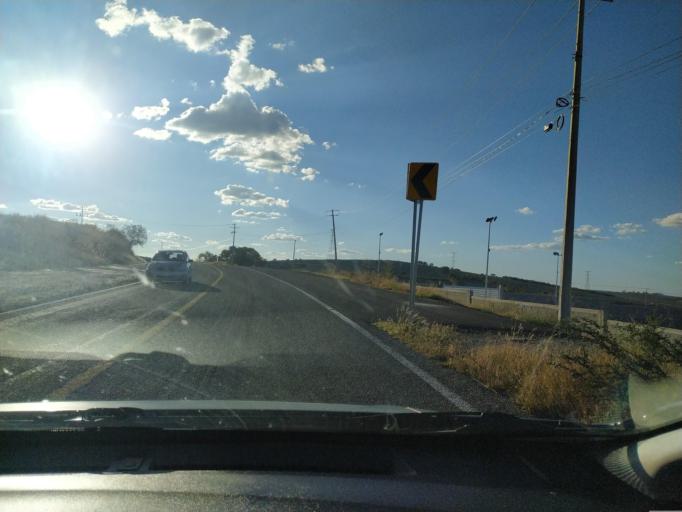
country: MX
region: Guanajuato
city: San Francisco del Rincon
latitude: 21.0374
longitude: -101.9101
